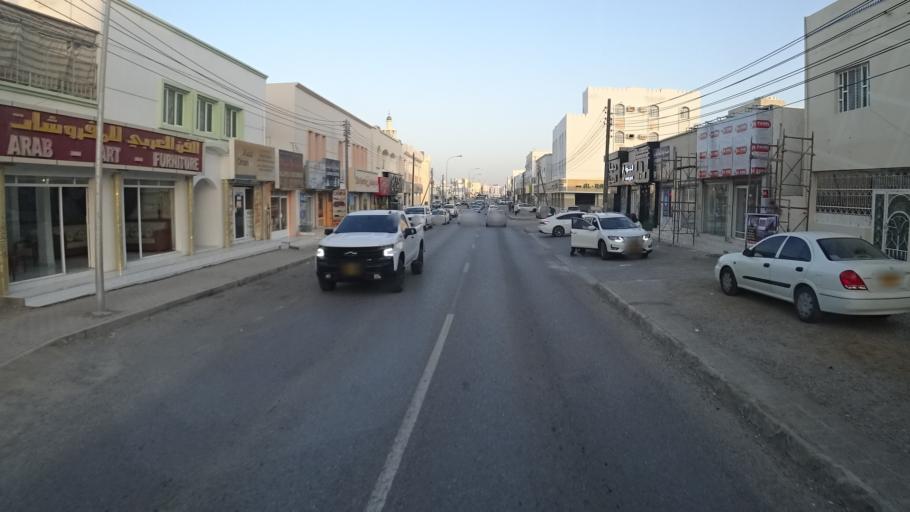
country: OM
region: Ash Sharqiyah
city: Sur
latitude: 22.5812
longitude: 59.5081
